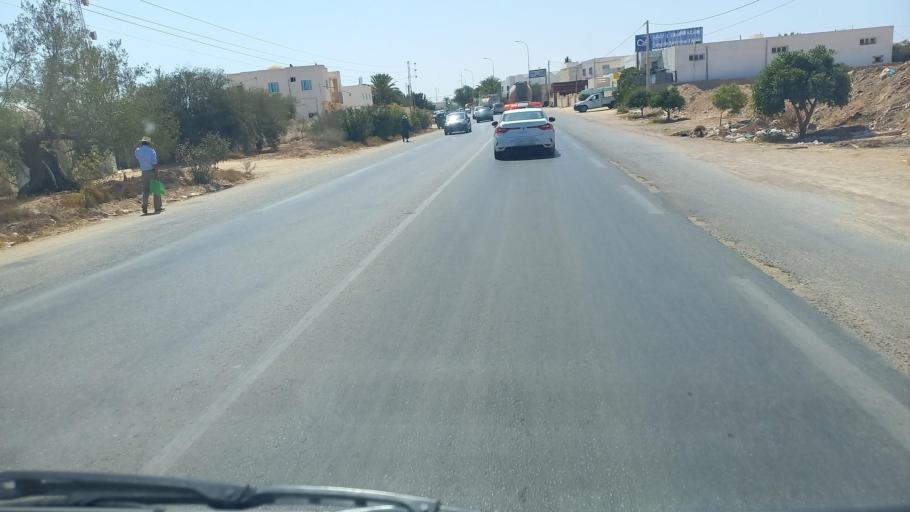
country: TN
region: Madanin
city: Houmt Souk
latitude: 33.8059
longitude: 10.8814
